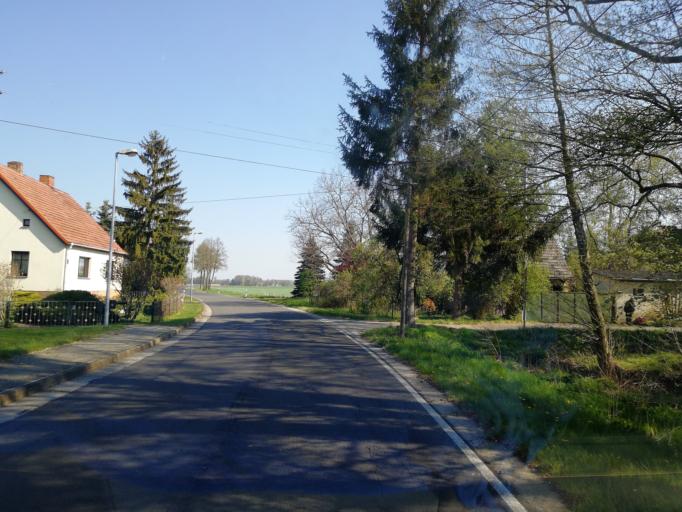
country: DE
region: Brandenburg
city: Crinitz
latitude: 51.7403
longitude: 13.8521
